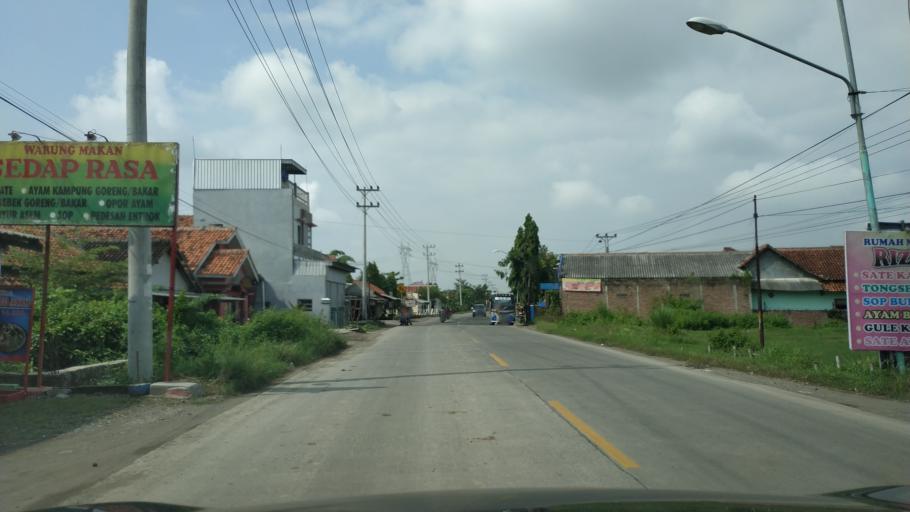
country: ID
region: Central Java
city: Ketanggungan
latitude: -6.9065
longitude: 108.8890
